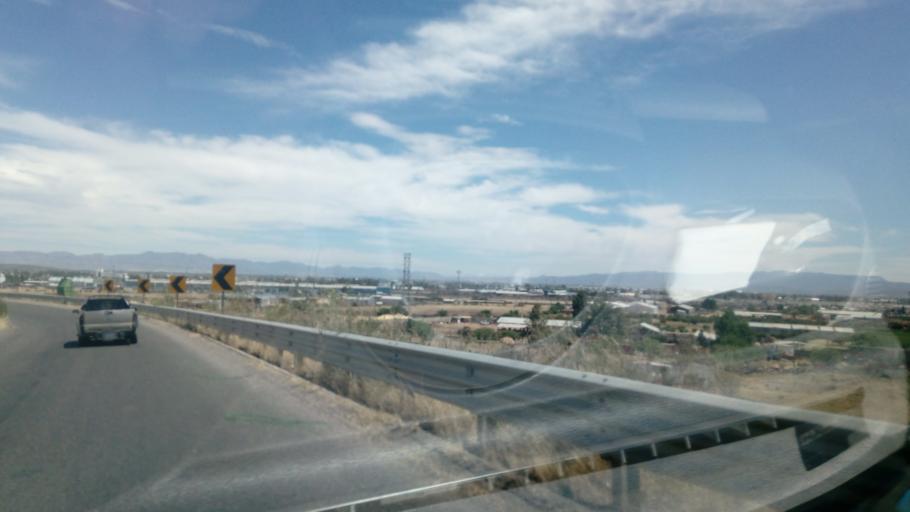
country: MX
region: Durango
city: Victoria de Durango
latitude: 24.0755
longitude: -104.6200
